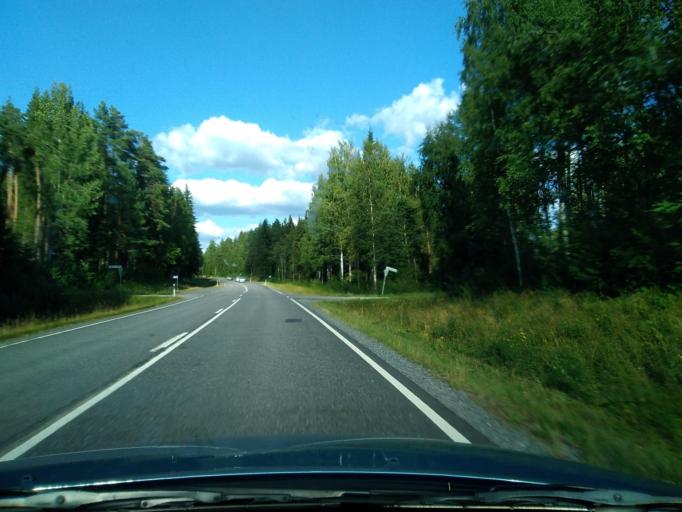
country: FI
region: Pirkanmaa
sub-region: Ylae-Pirkanmaa
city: Maenttae
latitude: 61.9831
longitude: 24.6239
